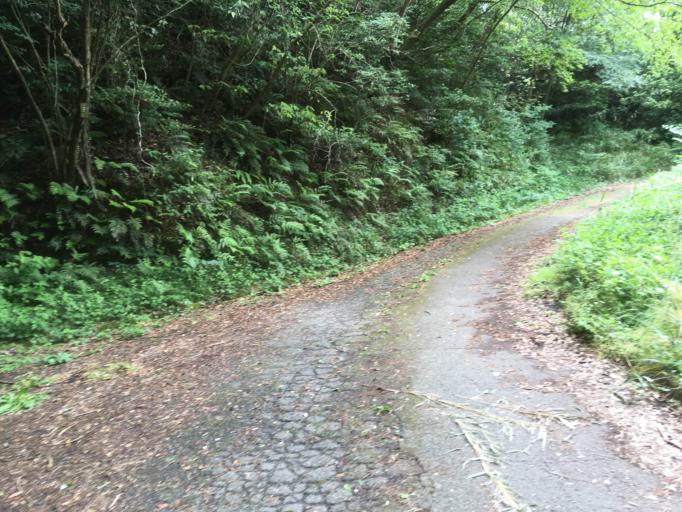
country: JP
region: Nara
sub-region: Ikoma-shi
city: Ikoma
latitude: 34.6924
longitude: 135.6704
